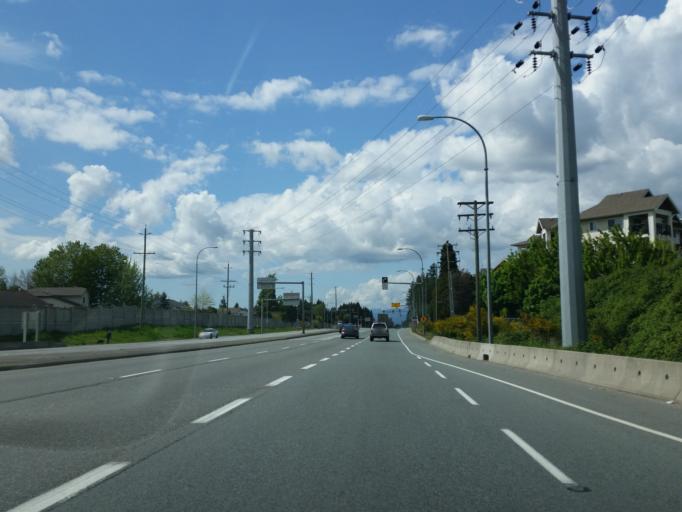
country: CA
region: British Columbia
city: Pitt Meadows
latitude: 49.2247
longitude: -122.6727
